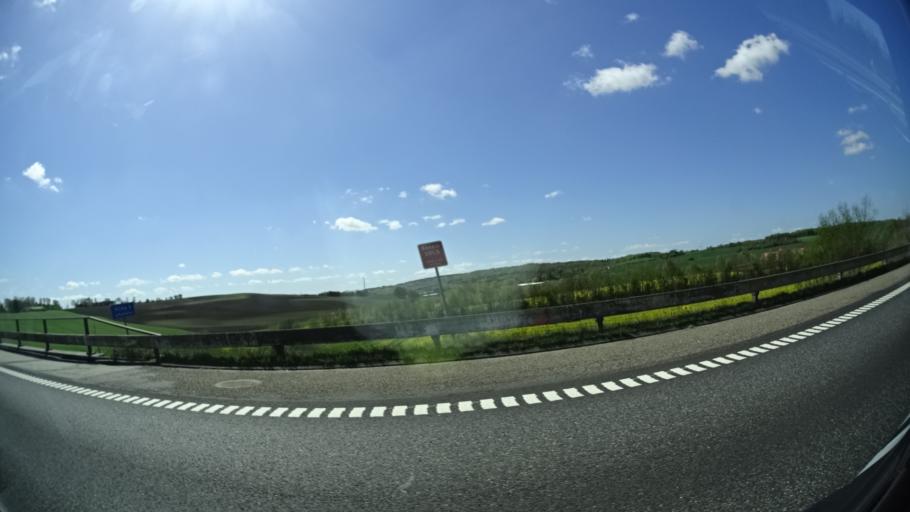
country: DK
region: Central Jutland
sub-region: Randers Kommune
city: Assentoft
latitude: 56.3918
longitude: 10.1008
